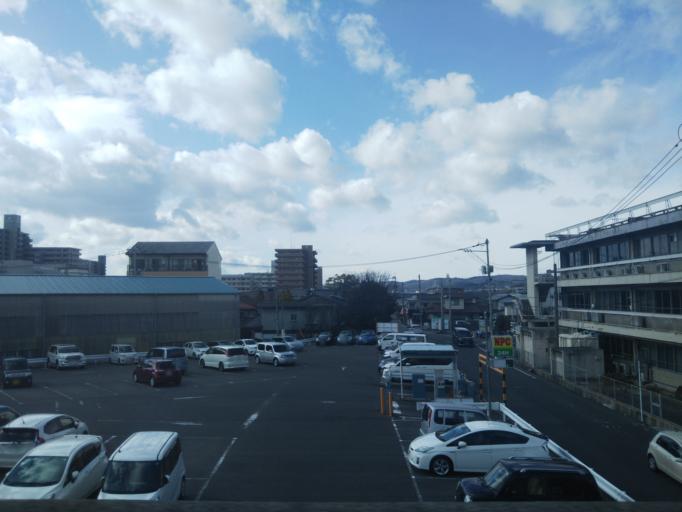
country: JP
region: Okayama
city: Okayama-shi
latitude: 34.6536
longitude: 133.9106
